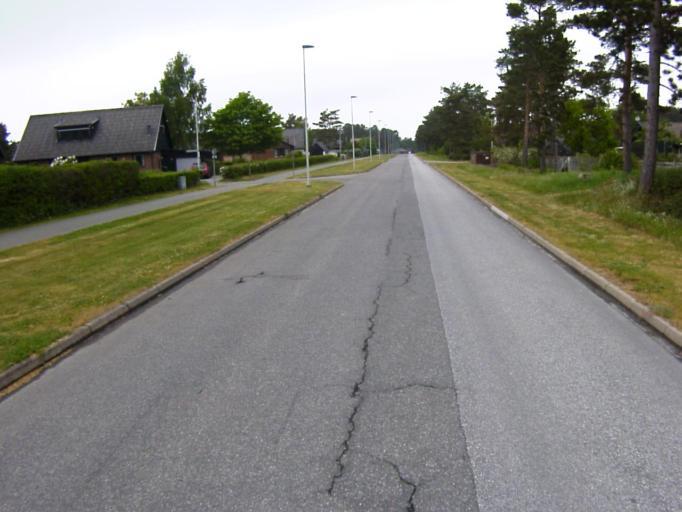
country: SE
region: Skane
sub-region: Kristianstads Kommun
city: Ahus
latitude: 55.9376
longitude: 14.2839
